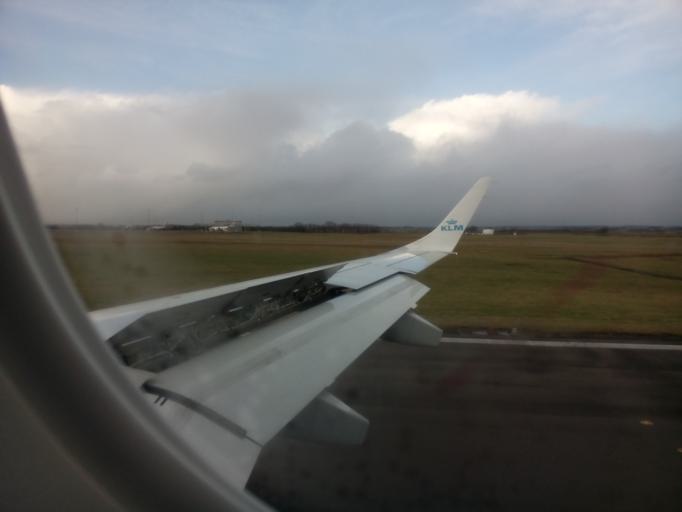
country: GB
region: England
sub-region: Newcastle upon Tyne
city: Dinnington
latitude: 55.0367
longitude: -1.6952
